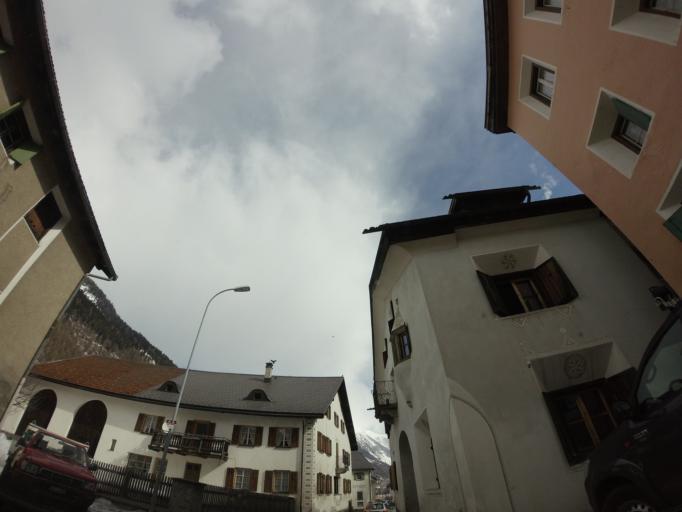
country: CH
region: Grisons
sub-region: Inn District
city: Zernez
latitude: 46.7500
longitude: 10.0796
